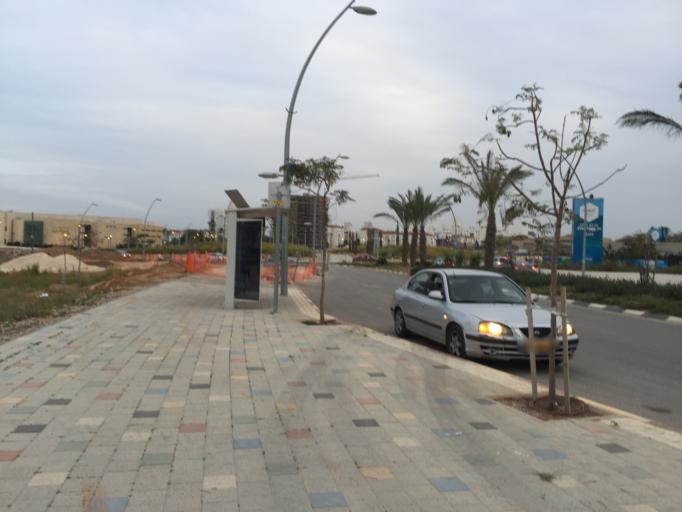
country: IL
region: Haifa
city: Qesarya
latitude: 32.5048
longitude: 34.9183
